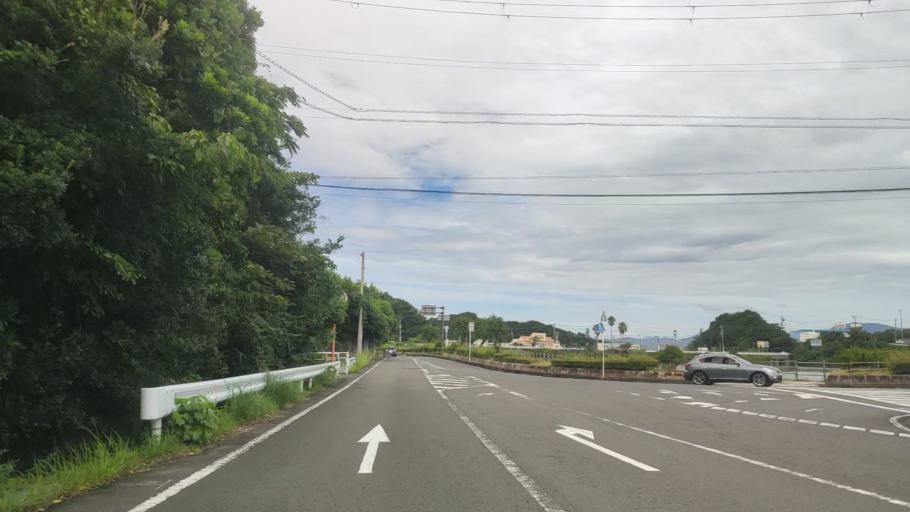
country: JP
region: Wakayama
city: Tanabe
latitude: 33.6908
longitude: 135.3878
